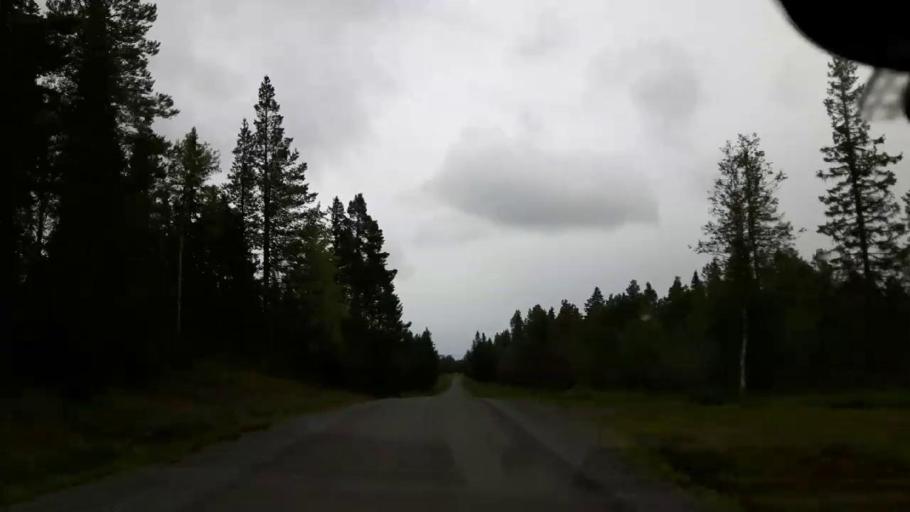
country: SE
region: Jaemtland
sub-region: OEstersunds Kommun
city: Ostersund
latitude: 63.0821
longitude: 14.5549
